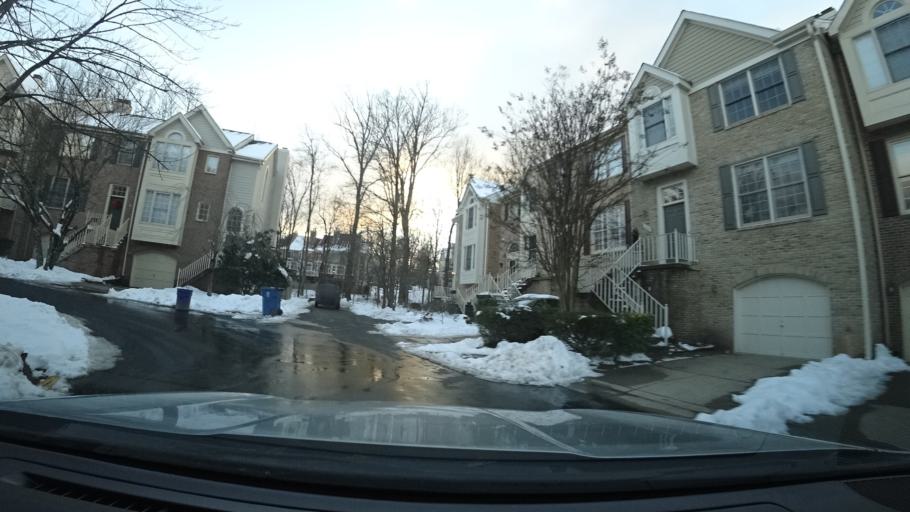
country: US
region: Virginia
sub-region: Fairfax County
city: Reston
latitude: 38.9814
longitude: -77.3407
